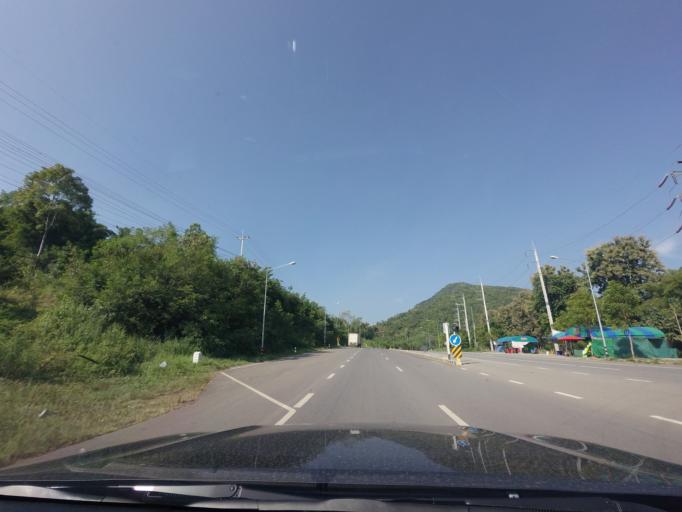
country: TH
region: Phetchabun
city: Lom Sak
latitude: 16.7625
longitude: 101.1456
